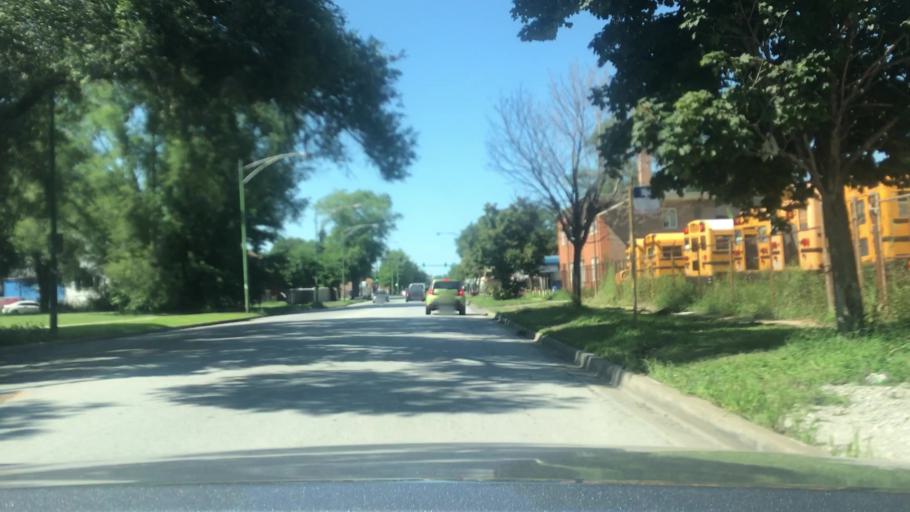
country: US
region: Indiana
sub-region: Lake County
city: Whiting
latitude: 41.7122
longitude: -87.5597
